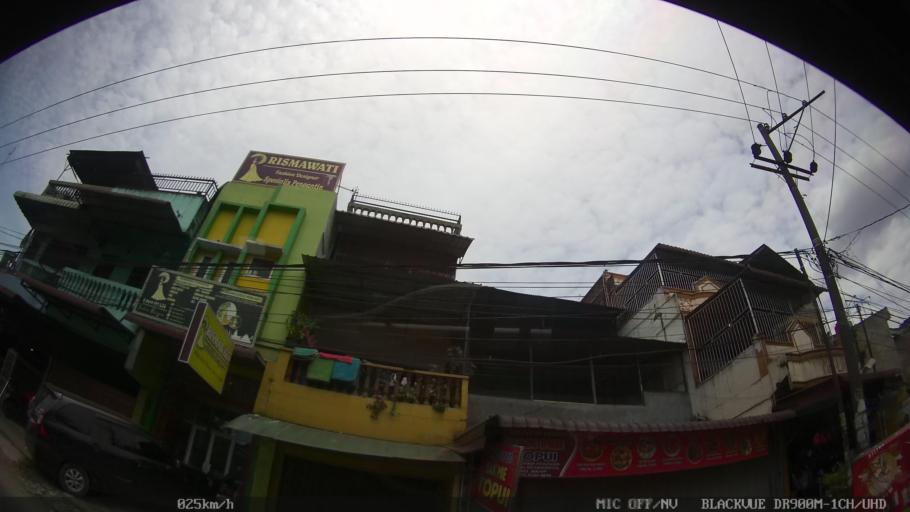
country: ID
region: North Sumatra
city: Deli Tua
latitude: 3.5381
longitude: 98.6517
